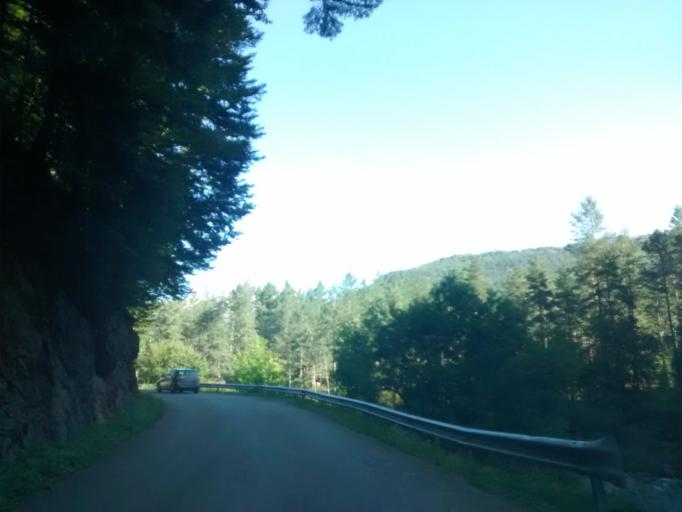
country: ES
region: Aragon
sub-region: Provincia de Huesca
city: Aragues del Puerto
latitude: 42.8293
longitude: -0.7114
